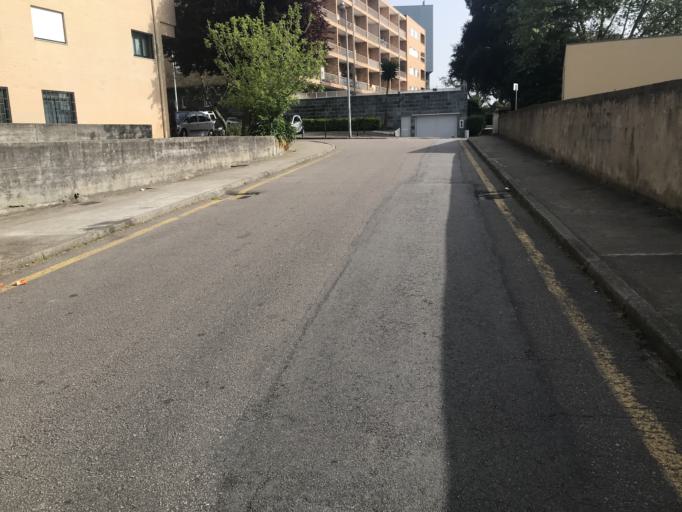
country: PT
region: Porto
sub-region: Matosinhos
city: Matosinhos
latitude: 41.1776
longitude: -8.6700
